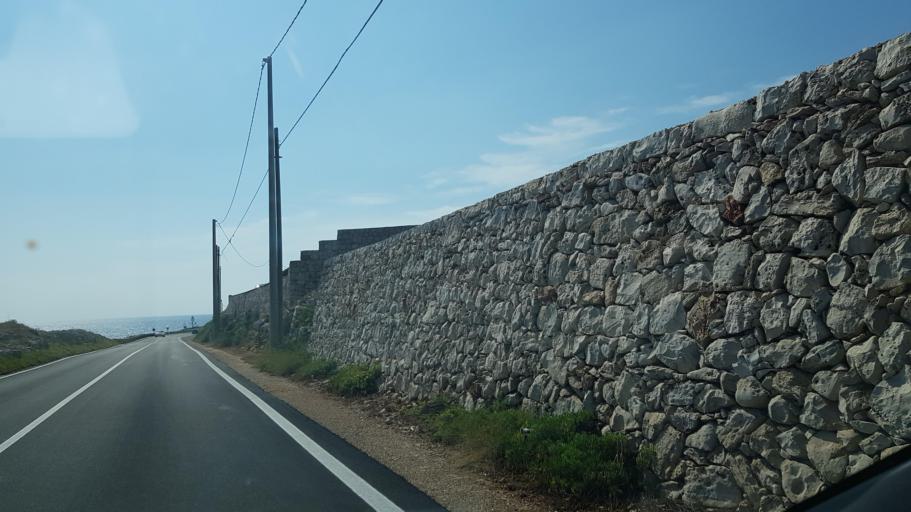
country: IT
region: Apulia
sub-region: Provincia di Lecce
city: Leuca
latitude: 39.7962
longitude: 18.3382
